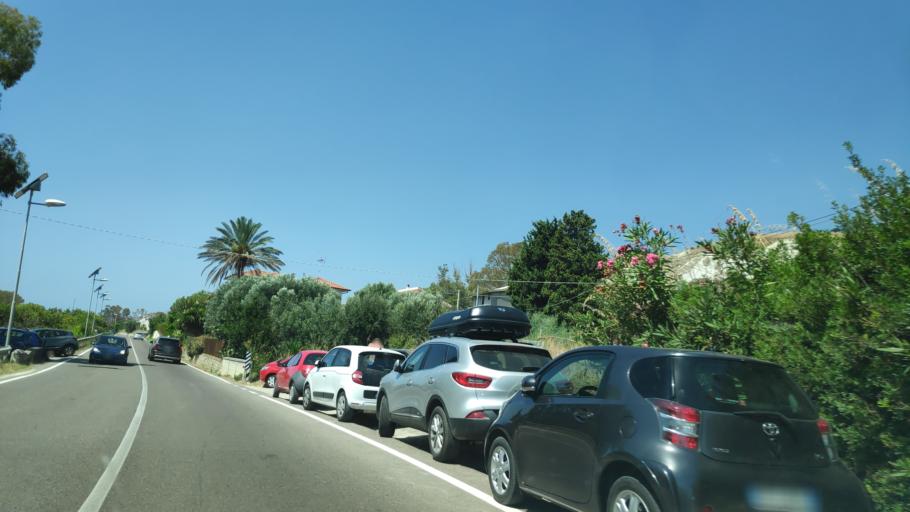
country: IT
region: Calabria
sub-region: Provincia di Reggio Calabria
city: Weather Station
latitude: 37.9243
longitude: 16.0504
